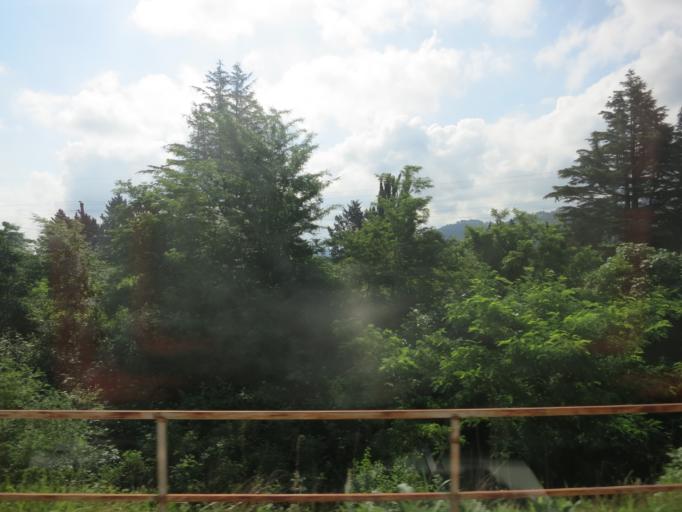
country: GE
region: Imereti
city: Samtredia
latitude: 42.1124
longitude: 42.3265
